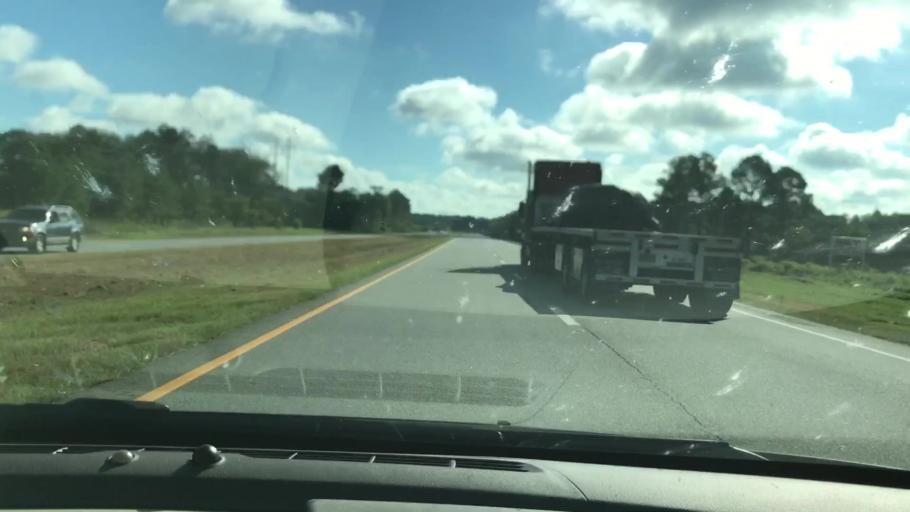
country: US
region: Georgia
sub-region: Worth County
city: Sylvester
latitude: 31.5507
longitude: -83.9603
